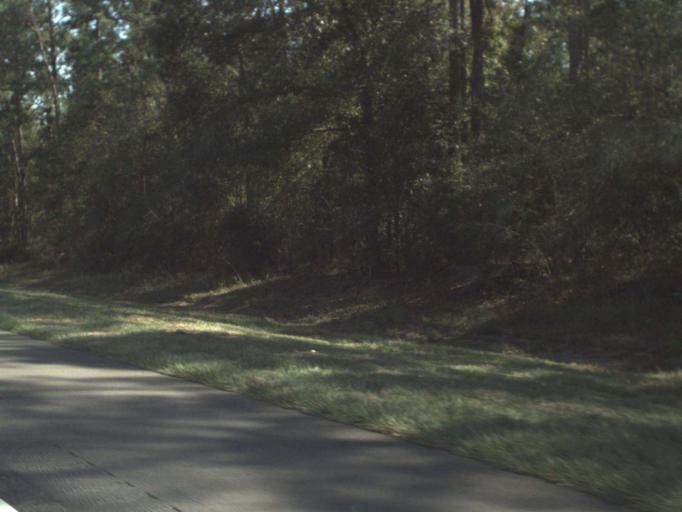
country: US
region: Florida
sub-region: Holmes County
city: Bonifay
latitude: 30.7610
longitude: -85.6533
